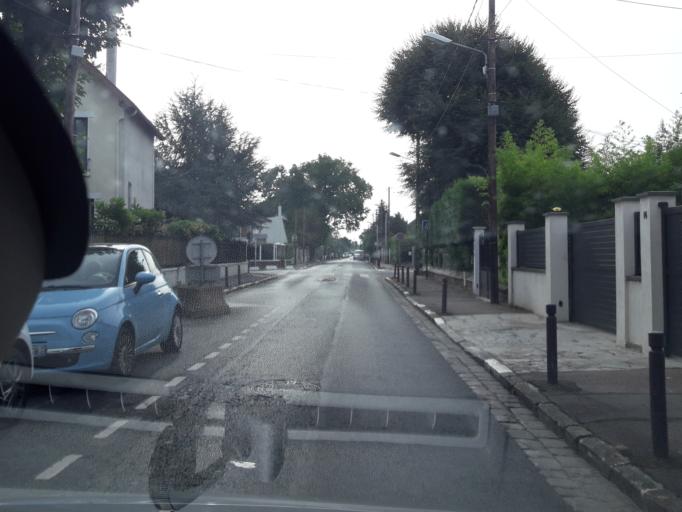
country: FR
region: Ile-de-France
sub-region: Departement de l'Essonne
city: Villemoisson-sur-Orge
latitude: 48.6498
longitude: 2.3381
